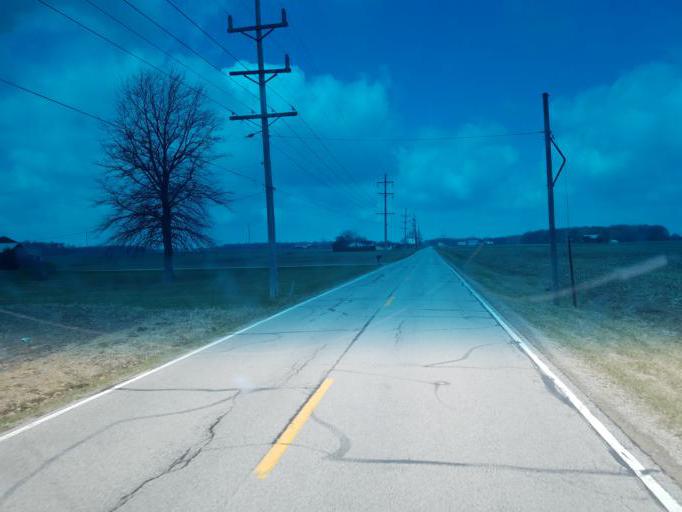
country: US
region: Ohio
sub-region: Crawford County
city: Galion
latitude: 40.7848
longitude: -82.8254
